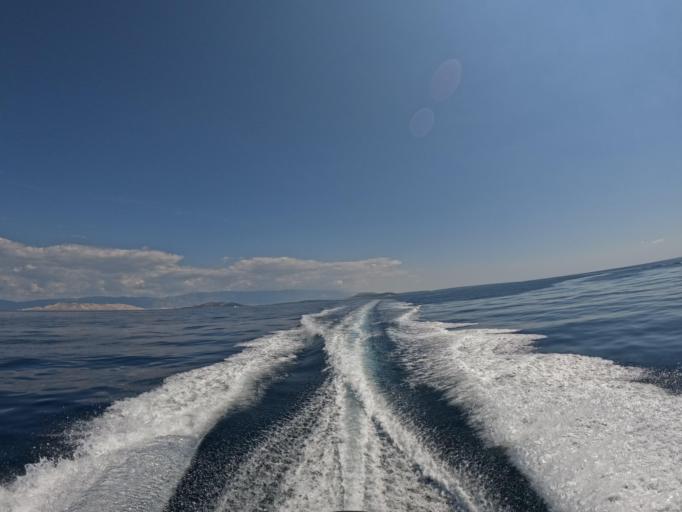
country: HR
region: Primorsko-Goranska
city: Punat
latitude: 44.9010
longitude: 14.6127
